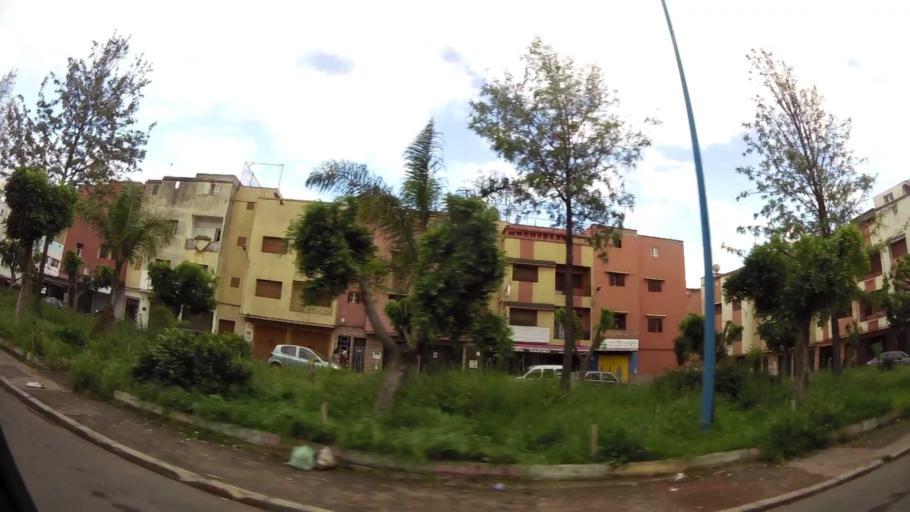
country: MA
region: Grand Casablanca
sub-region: Mohammedia
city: Mohammedia
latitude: 33.6802
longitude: -7.3939
